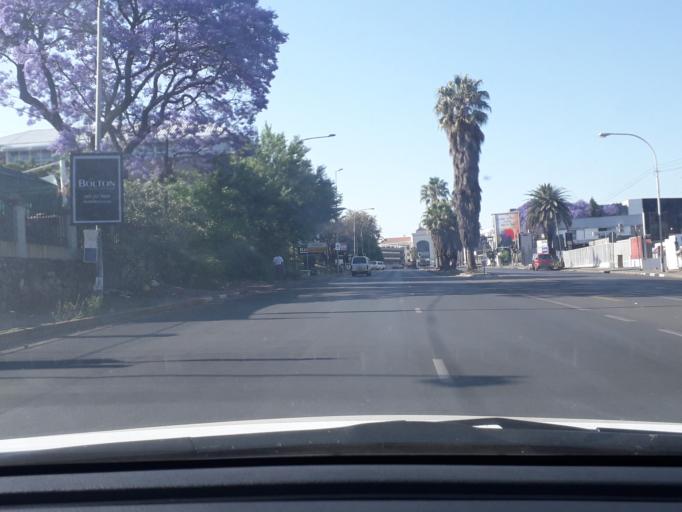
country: ZA
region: Gauteng
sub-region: City of Johannesburg Metropolitan Municipality
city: Johannesburg
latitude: -26.1421
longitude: 28.0357
